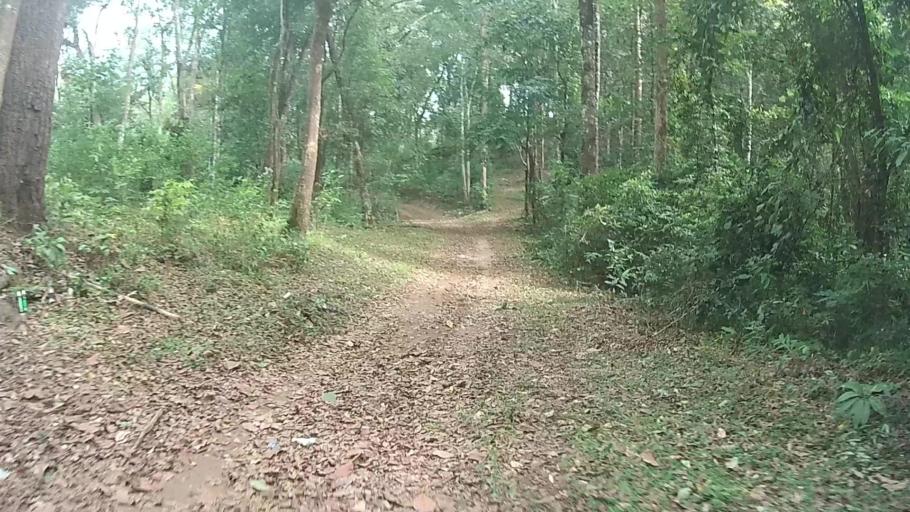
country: TH
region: Chiang Mai
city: Mae On
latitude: 18.8014
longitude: 99.3576
